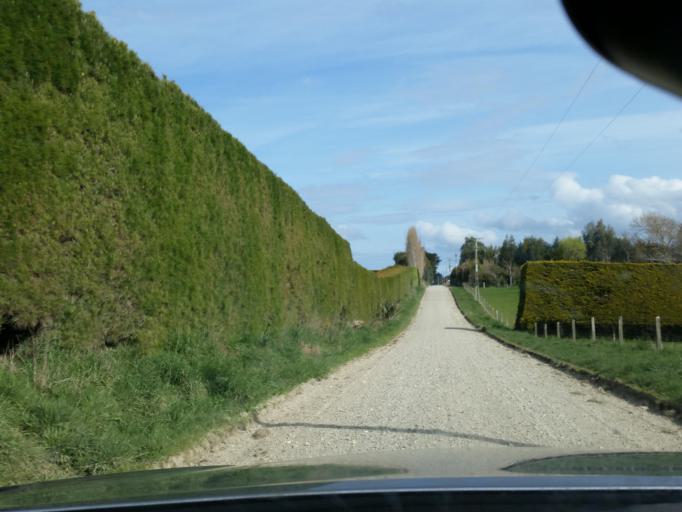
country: NZ
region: Southland
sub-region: Invercargill City
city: Invercargill
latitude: -46.3084
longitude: 168.4789
